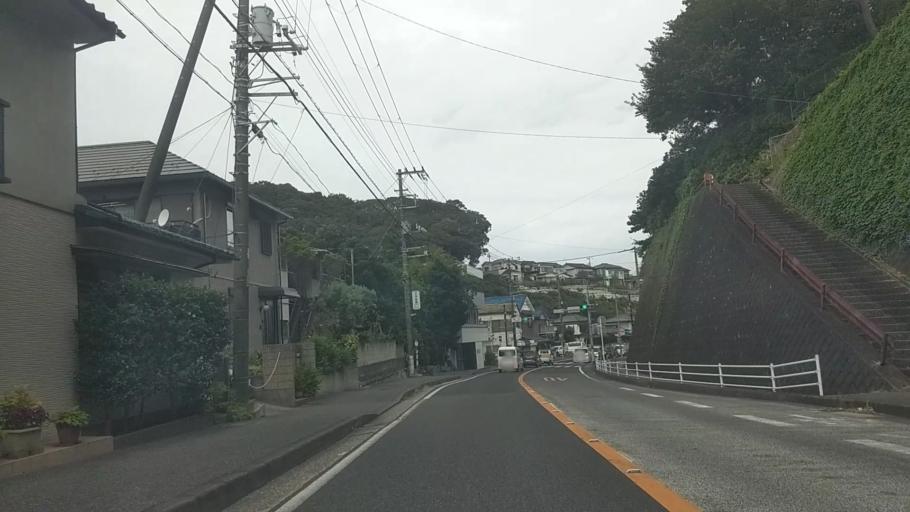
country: JP
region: Kanagawa
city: Yokosuka
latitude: 35.2459
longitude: 139.7249
